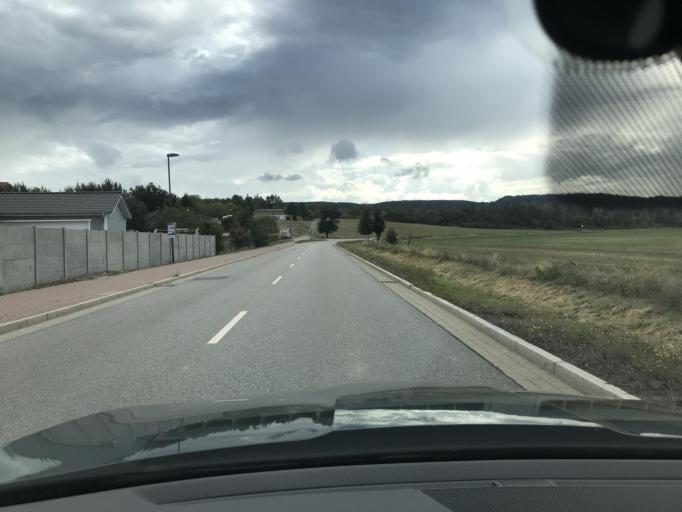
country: DE
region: Saxony-Anhalt
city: Thale
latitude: 51.7715
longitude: 11.0534
